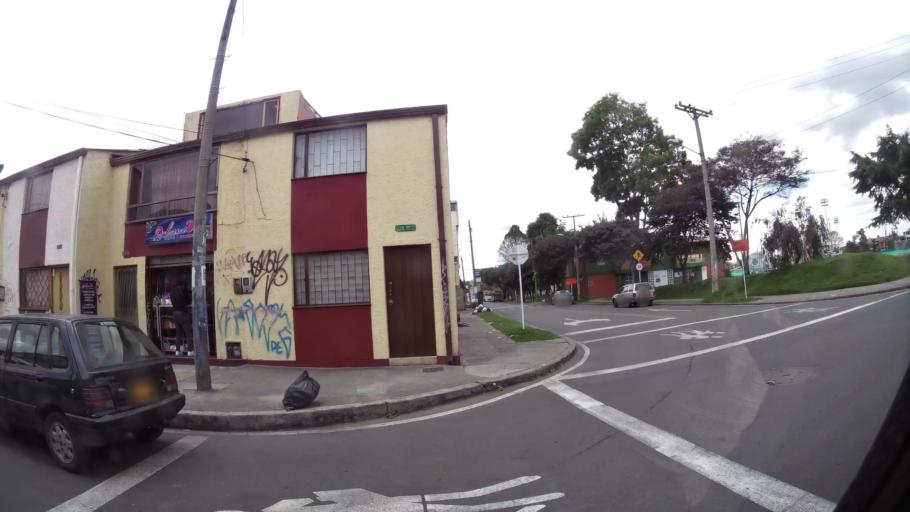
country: CO
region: Cundinamarca
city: Funza
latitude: 4.7163
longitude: -74.1211
